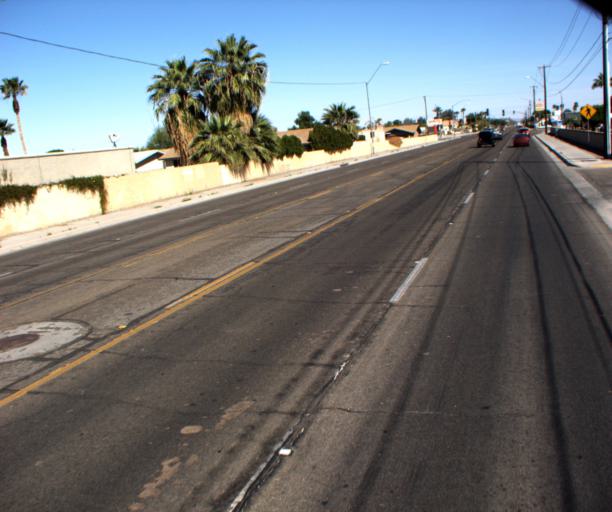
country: US
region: Arizona
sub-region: Yuma County
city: Yuma
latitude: 32.6894
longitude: -114.6503
